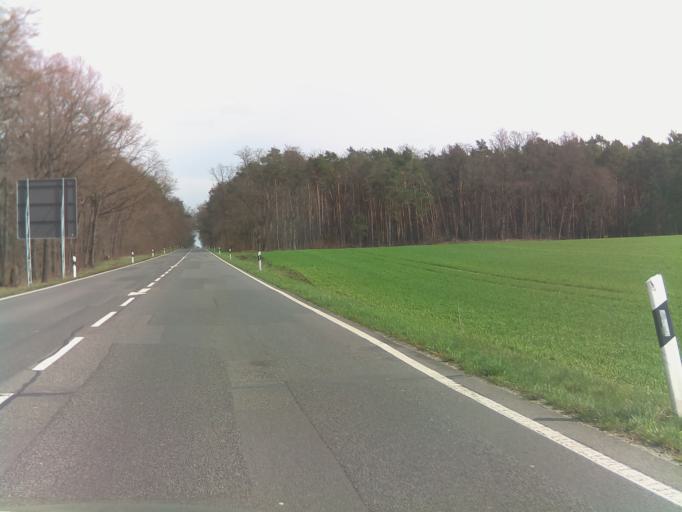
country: DE
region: Brandenburg
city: Werben
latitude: 51.7575
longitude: 14.1653
